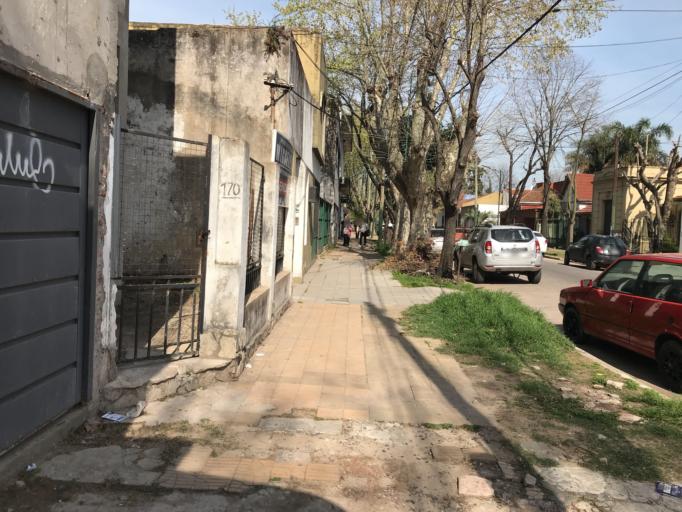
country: AR
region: Buenos Aires
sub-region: Partido de Lomas de Zamora
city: Lomas de Zamora
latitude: -34.7680
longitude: -58.3989
